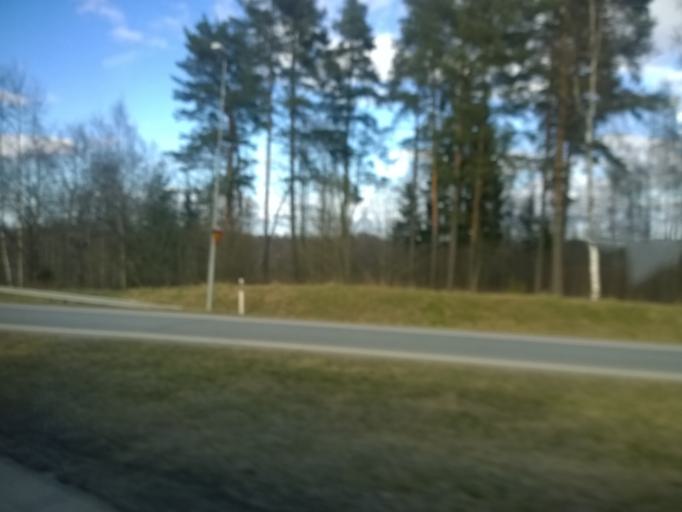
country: FI
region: Pirkanmaa
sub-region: Tampere
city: Tampere
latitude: 61.4696
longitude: 23.8409
